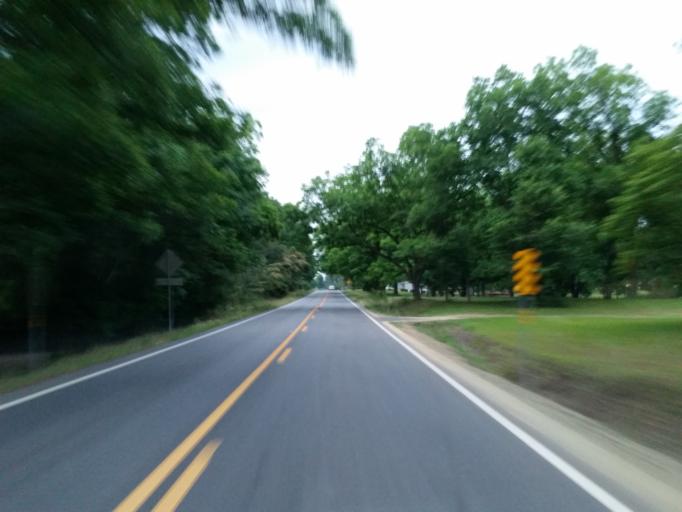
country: US
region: Georgia
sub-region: Turner County
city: Ashburn
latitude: 31.7794
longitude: -83.6960
